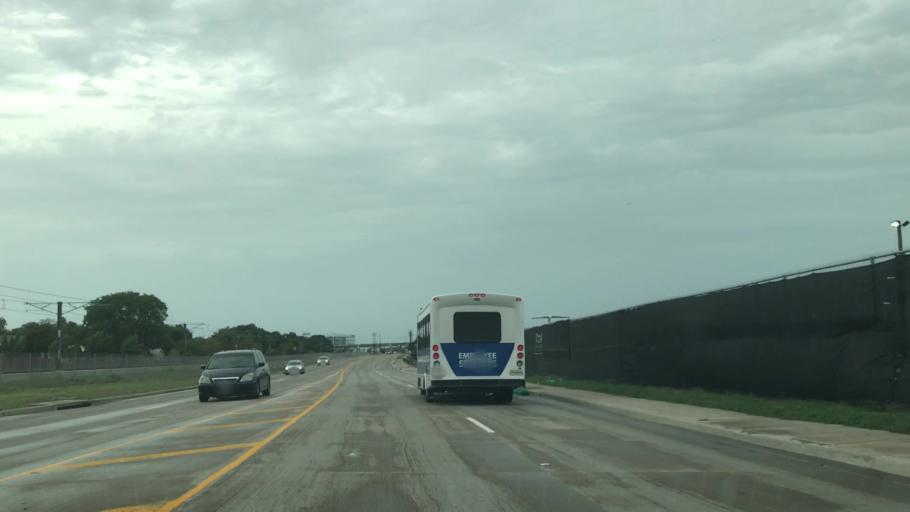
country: US
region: Texas
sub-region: Dallas County
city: University Park
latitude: 32.8395
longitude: -96.8537
